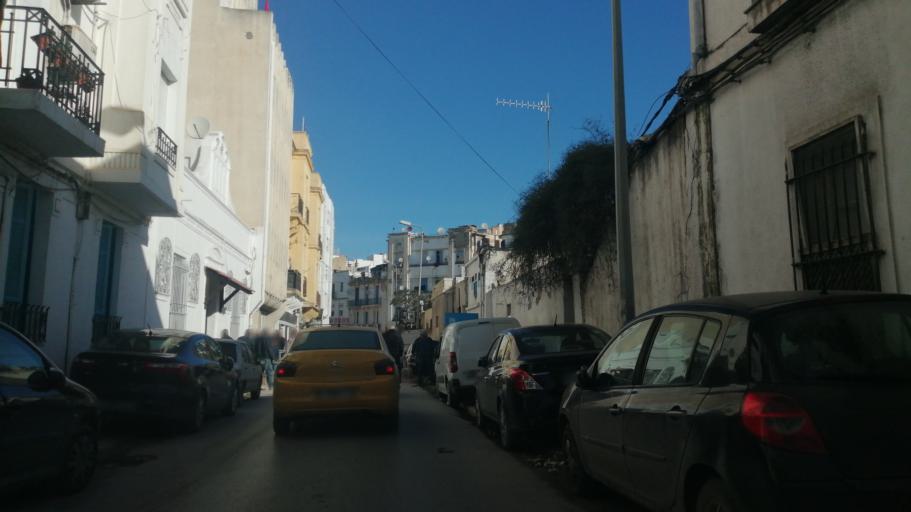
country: TN
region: Tunis
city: Tunis
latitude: 36.8080
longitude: 10.1791
